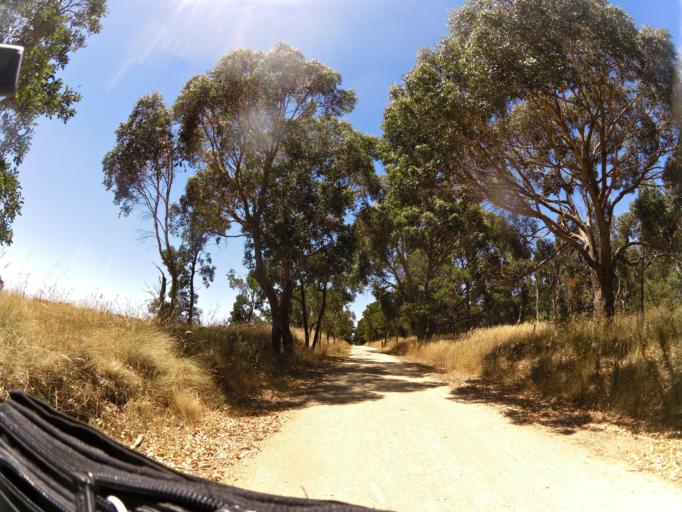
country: AU
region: Victoria
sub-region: Ballarat North
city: Delacombe
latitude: -37.5568
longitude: 143.7462
